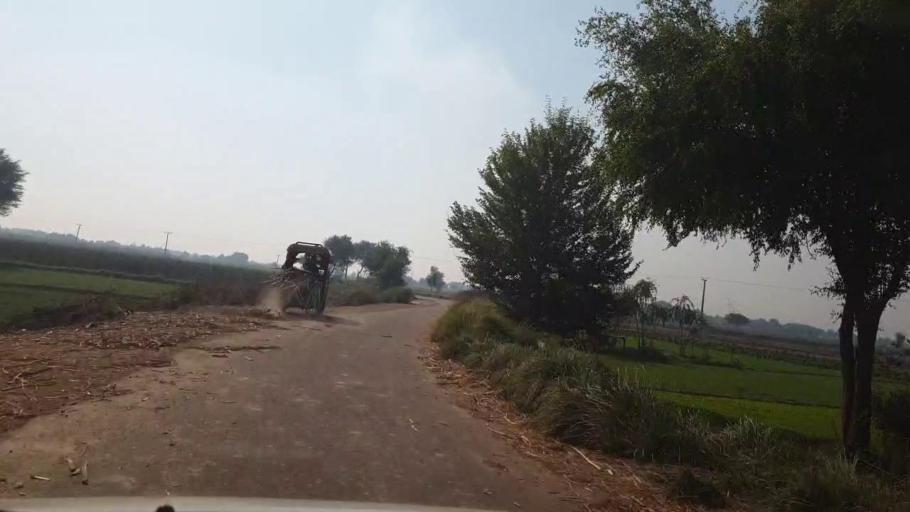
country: PK
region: Sindh
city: Bhan
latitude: 26.6090
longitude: 67.7601
